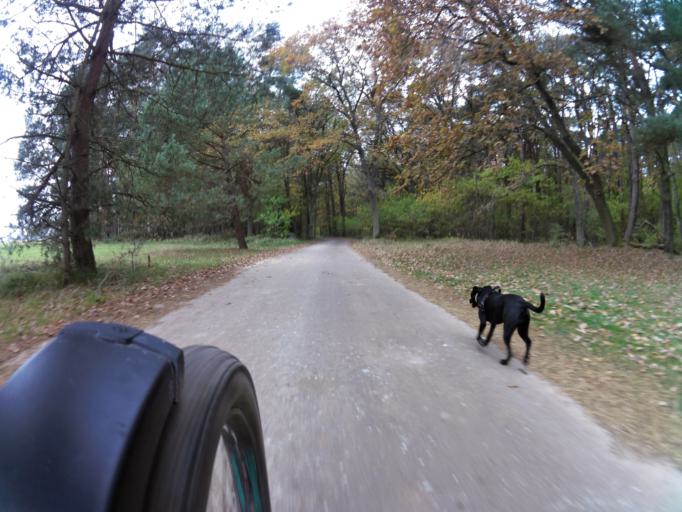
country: PL
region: Pomeranian Voivodeship
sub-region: Powiat pucki
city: Krokowa
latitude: 54.8295
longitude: 18.1409
